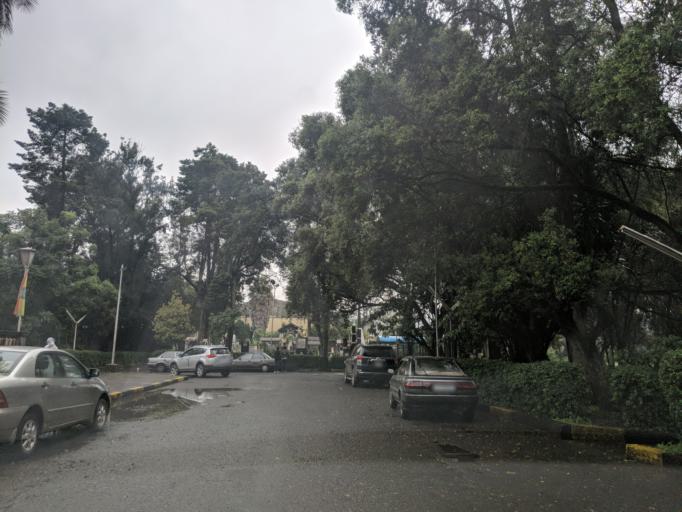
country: ET
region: Adis Abeba
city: Addis Ababa
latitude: 9.0307
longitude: 38.7670
